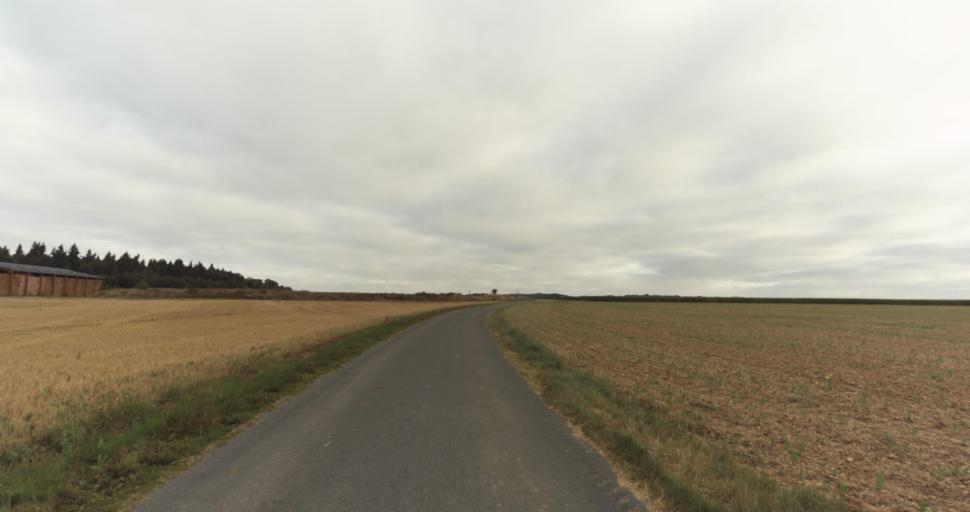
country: FR
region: Haute-Normandie
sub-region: Departement de l'Eure
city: Saint-Germain-sur-Avre
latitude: 48.7820
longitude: 1.2605
